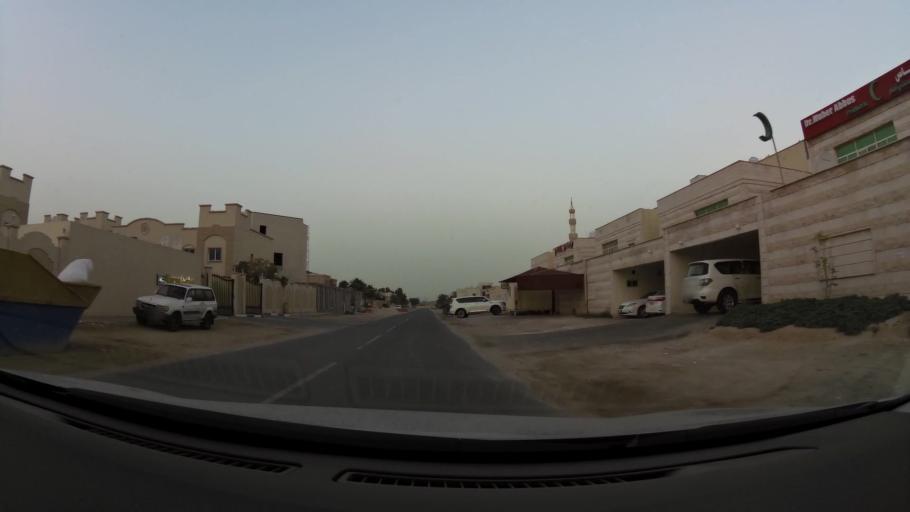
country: QA
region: Baladiyat ar Rayyan
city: Ar Rayyan
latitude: 25.2526
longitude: 51.4618
